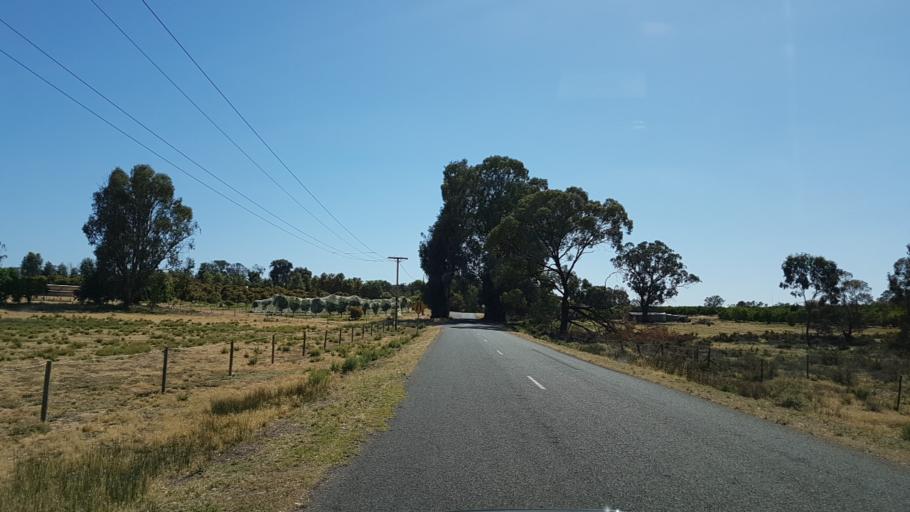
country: AU
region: South Australia
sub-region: Loxton Waikerie
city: Waikerie
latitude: -34.1665
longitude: 140.0276
